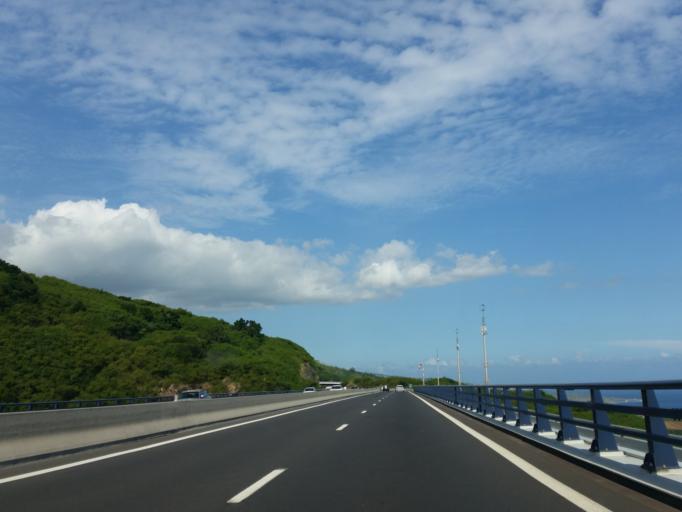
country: RE
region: Reunion
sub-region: Reunion
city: Trois-Bassins
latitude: -21.1217
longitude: 55.2794
